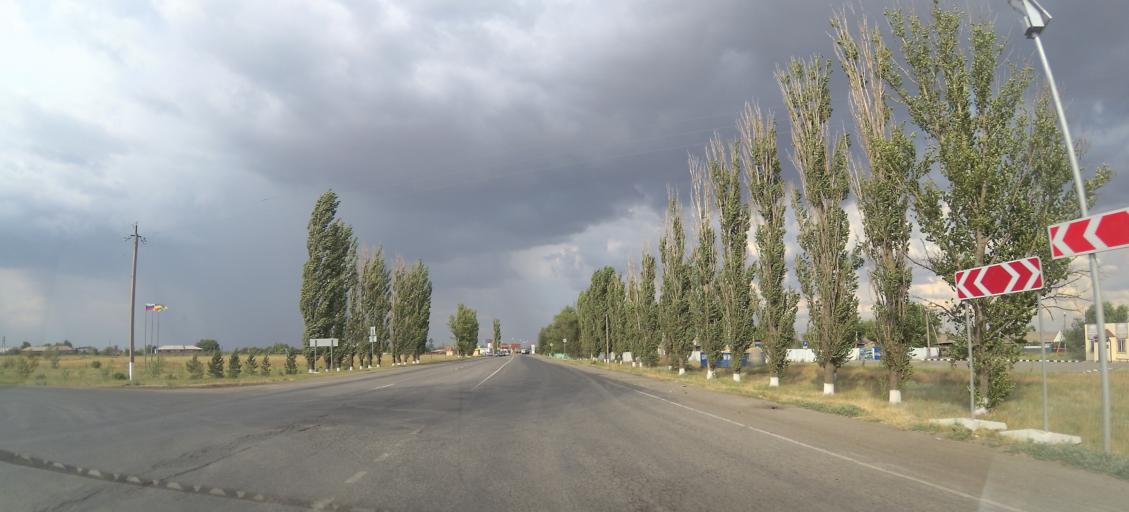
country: RU
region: Rostov
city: Zimovniki
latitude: 47.1427
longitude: 42.4389
